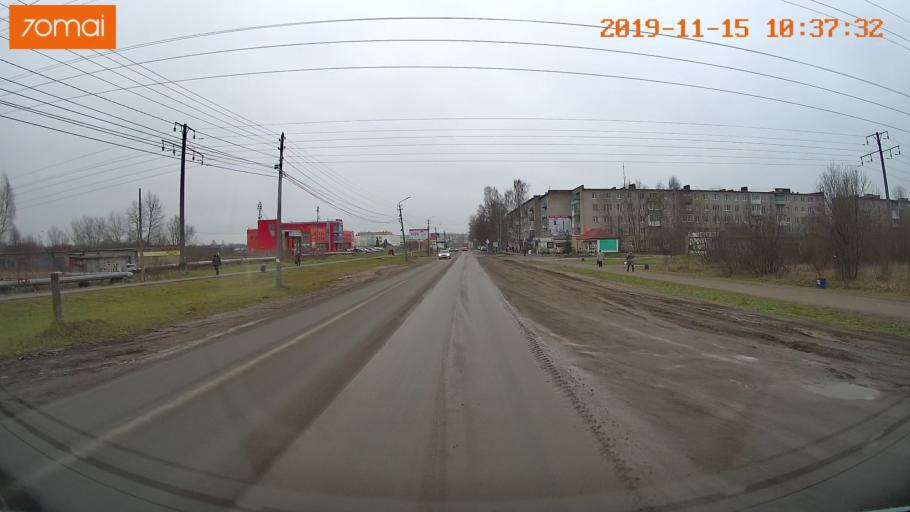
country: RU
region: Vologda
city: Sheksna
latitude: 59.2322
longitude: 38.5128
